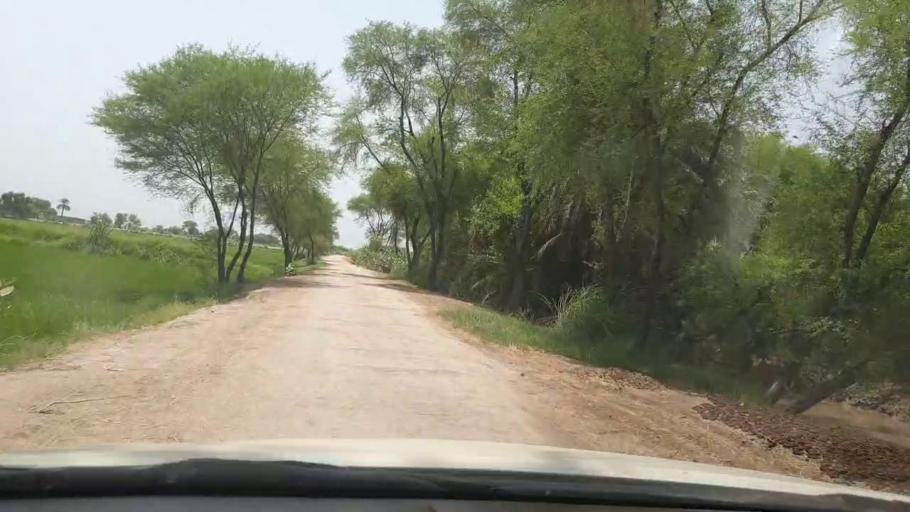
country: PK
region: Sindh
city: Shikarpur
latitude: 28.0726
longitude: 68.5395
